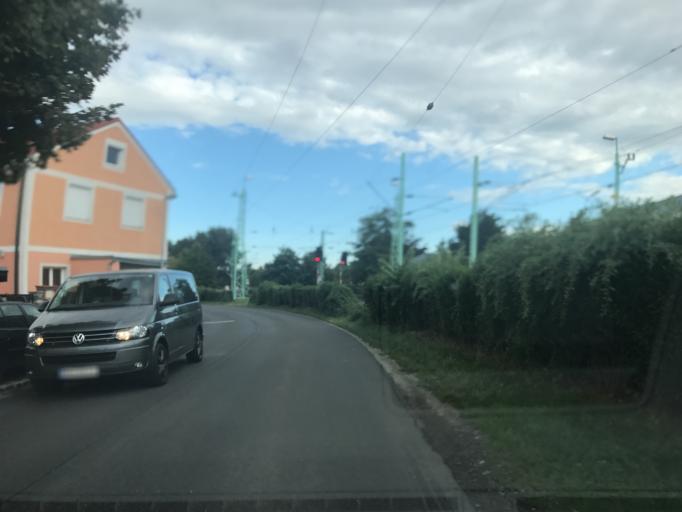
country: AT
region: Burgenland
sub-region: Eisenstadt-Umgebung
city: Neufeld an der Leitha
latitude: 47.8666
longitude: 16.3831
